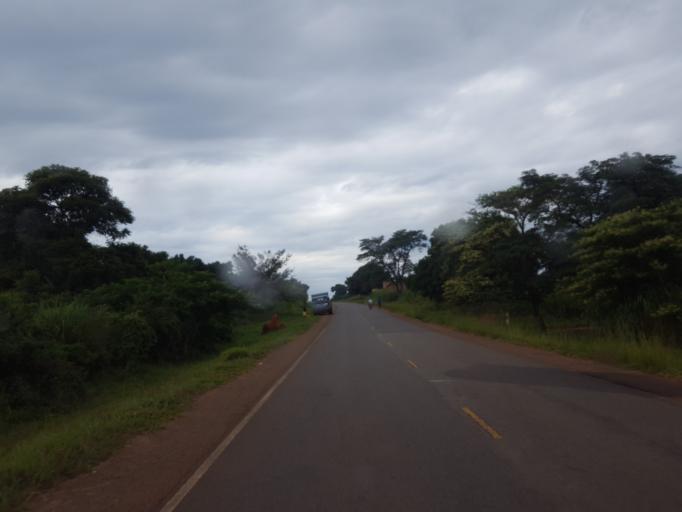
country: UG
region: Central Region
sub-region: Kiboga District
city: Kiboga
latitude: 1.0023
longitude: 31.6986
